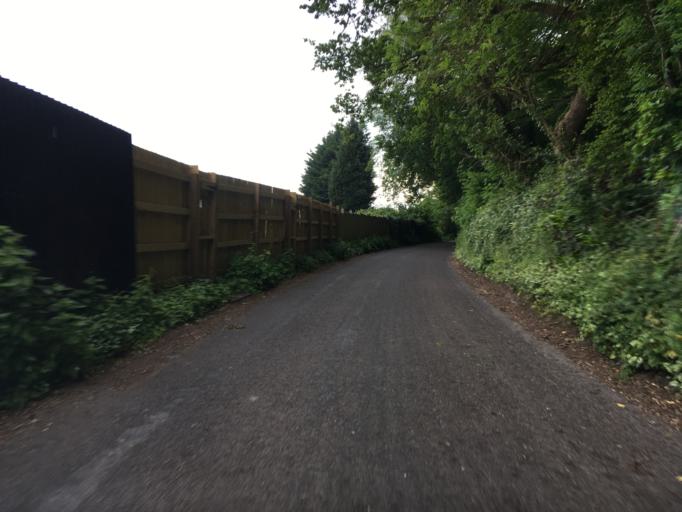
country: GB
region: England
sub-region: North Somerset
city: Clevedon
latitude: 51.4467
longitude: -2.8372
